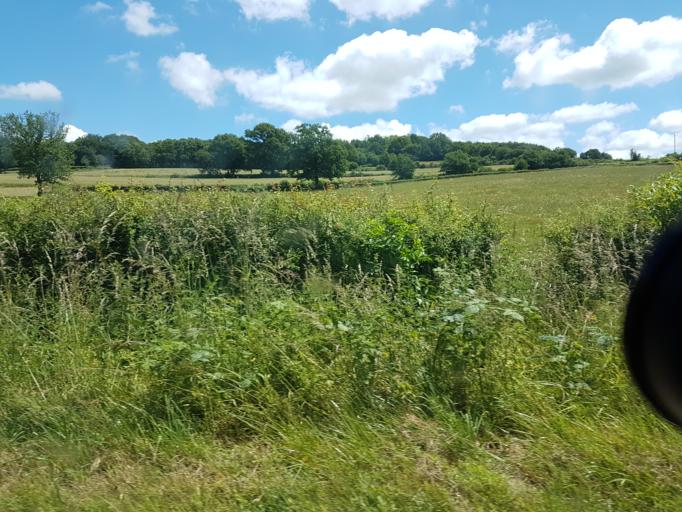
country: FR
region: Bourgogne
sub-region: Departement de Saone-et-Loire
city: Curgy
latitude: 47.0235
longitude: 4.4346
